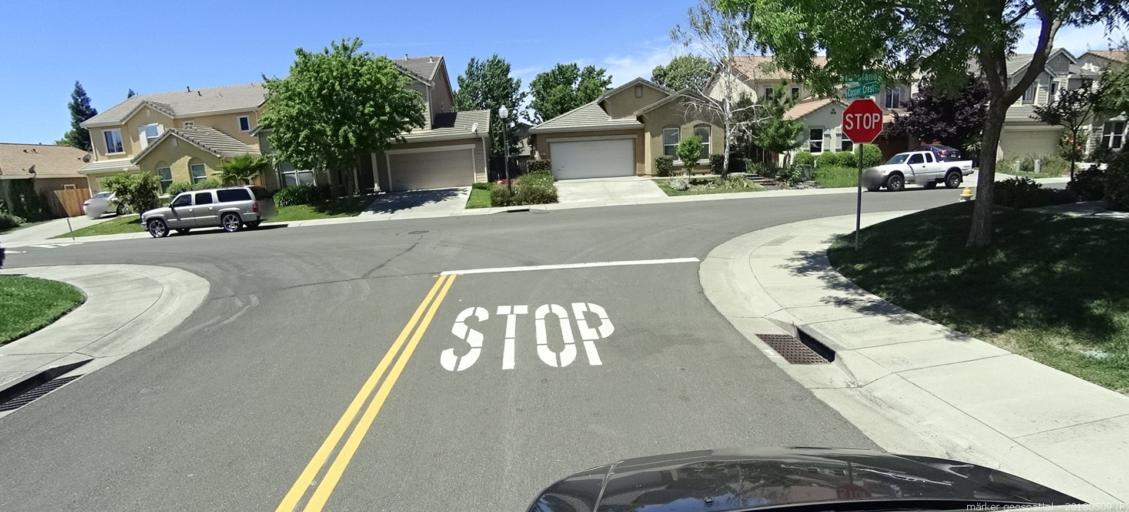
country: US
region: California
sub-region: Sacramento County
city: Sacramento
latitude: 38.6372
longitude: -121.5084
